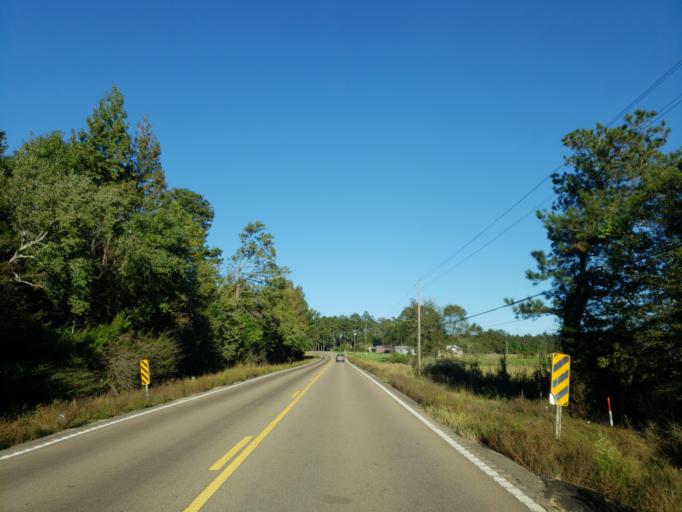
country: US
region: Mississippi
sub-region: Perry County
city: Richton
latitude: 31.3674
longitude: -88.8773
